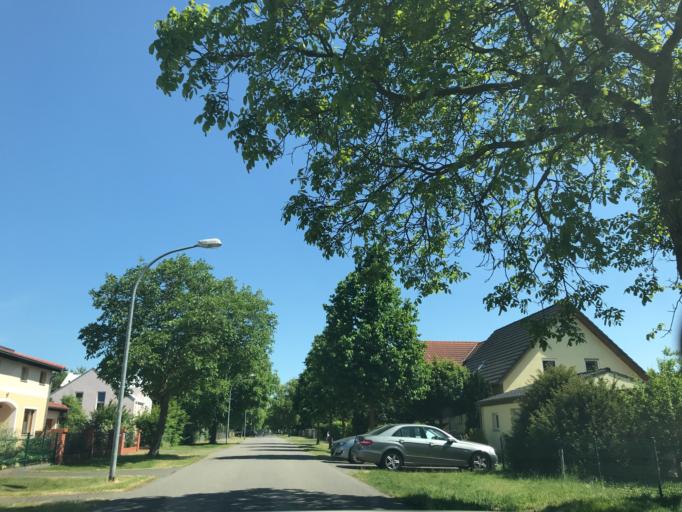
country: DE
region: Brandenburg
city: Falkensee
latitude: 52.5530
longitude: 13.0786
